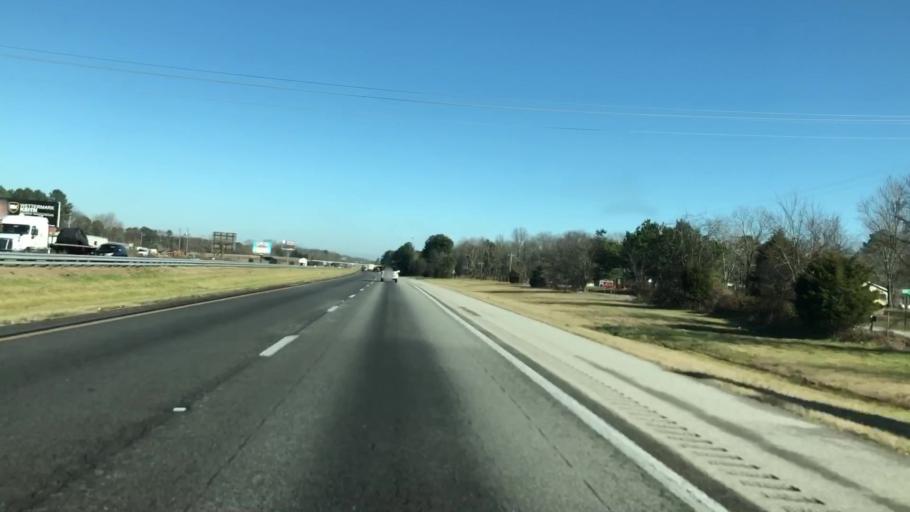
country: US
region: Alabama
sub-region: Limestone County
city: Athens
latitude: 34.8545
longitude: -86.9284
